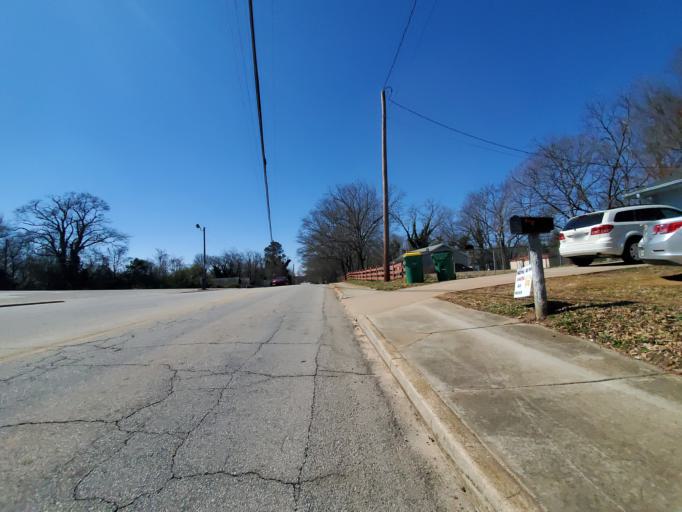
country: US
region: Georgia
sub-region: Barrow County
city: Winder
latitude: 33.9906
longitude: -83.7124
